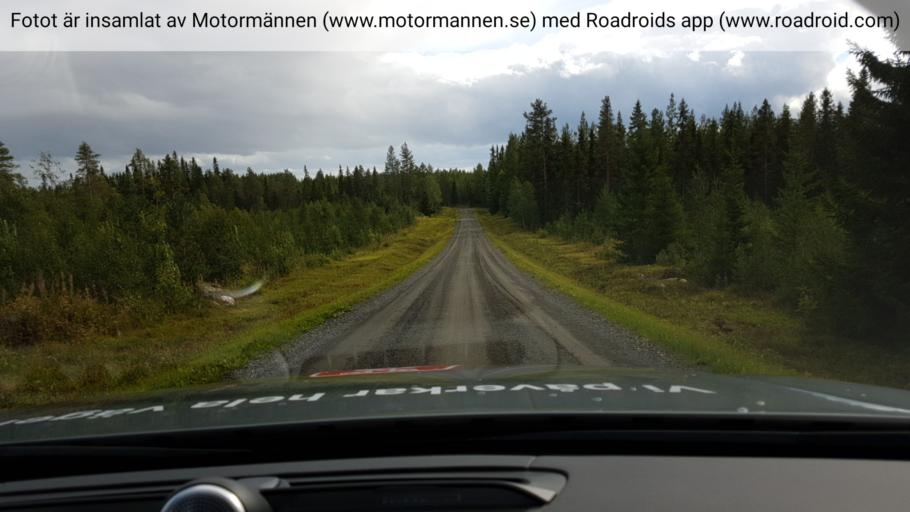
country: SE
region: Jaemtland
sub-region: OEstersunds Kommun
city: Lit
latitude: 63.7715
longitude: 14.6555
